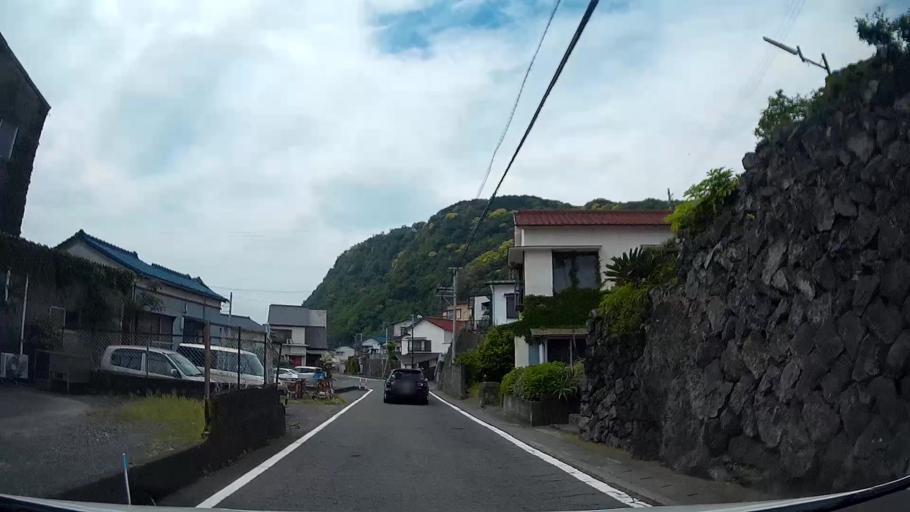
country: JP
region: Shizuoka
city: Ito
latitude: 34.9069
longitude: 139.1357
